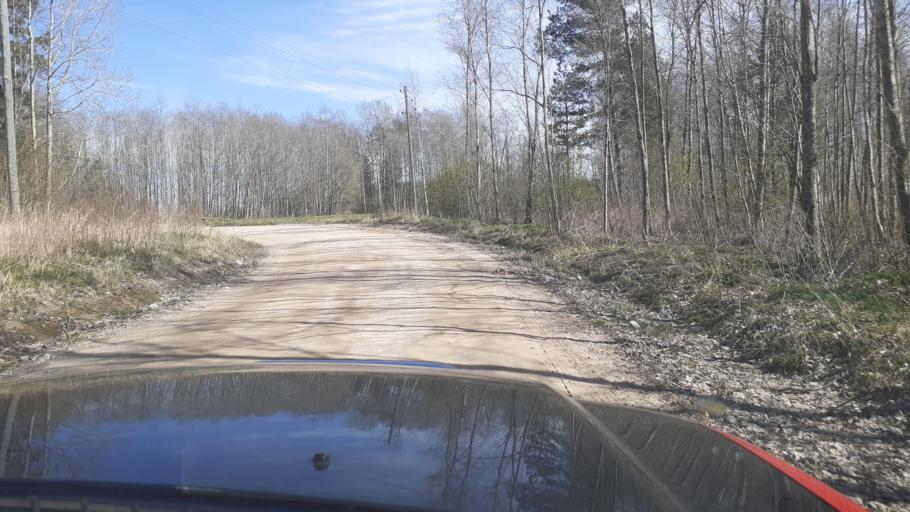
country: LV
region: Kuldigas Rajons
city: Kuldiga
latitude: 56.8454
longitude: 21.9765
